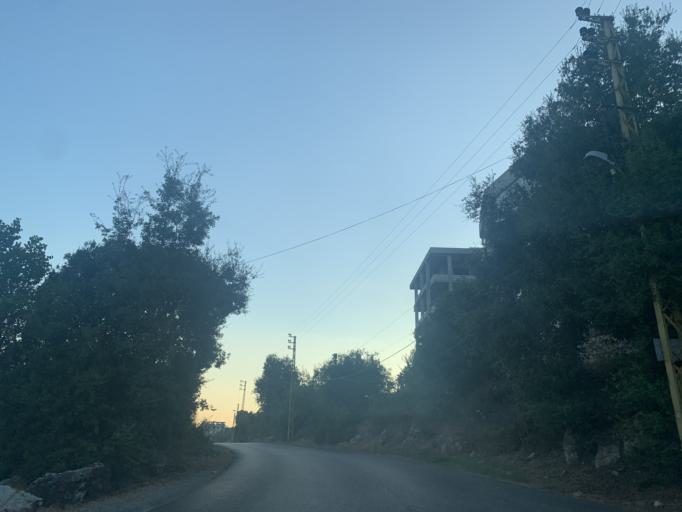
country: LB
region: Mont-Liban
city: Djounie
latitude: 33.9543
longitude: 35.6871
